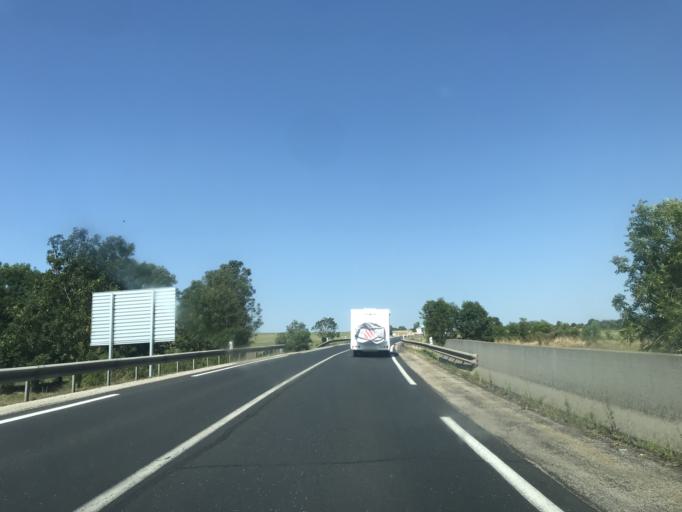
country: FR
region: Auvergne
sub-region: Departement de la Haute-Loire
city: Saint-Paulien
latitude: 45.1129
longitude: 3.7423
